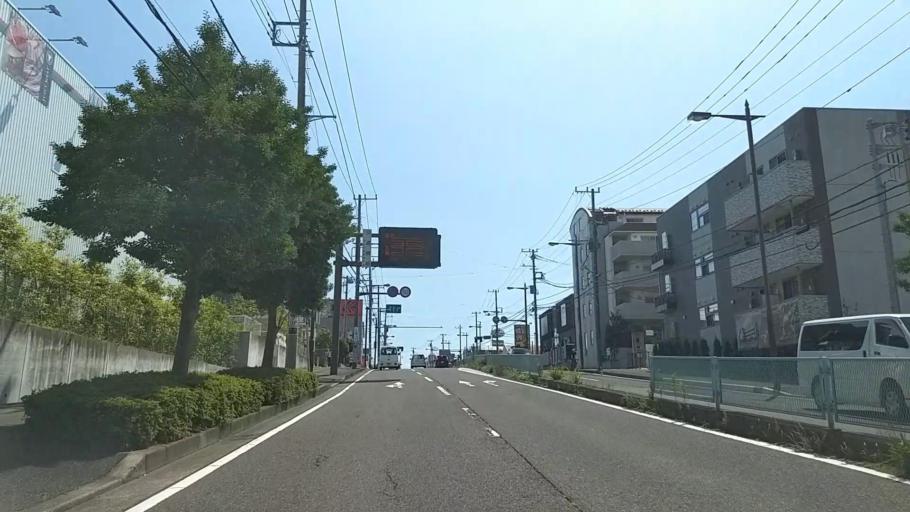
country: JP
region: Kanagawa
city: Fujisawa
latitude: 35.3555
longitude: 139.5030
